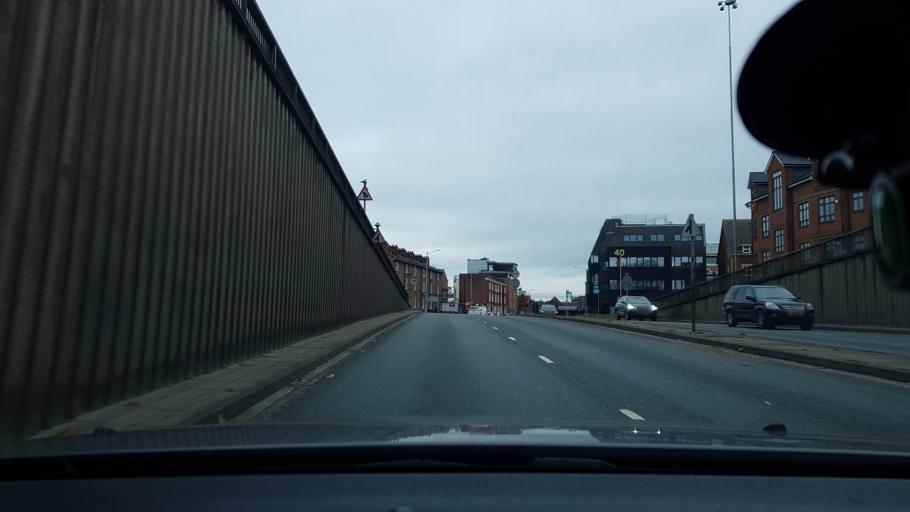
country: GB
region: England
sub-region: Reading
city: Reading
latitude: 51.4570
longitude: -0.9778
